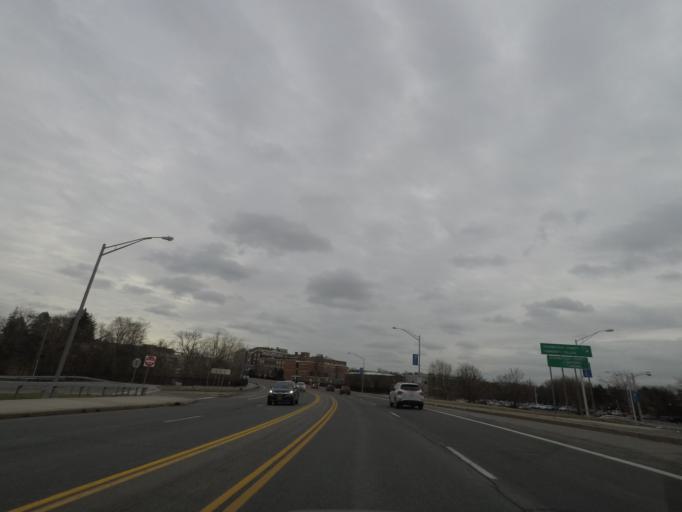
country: US
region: New York
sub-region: Schenectady County
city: Schenectady
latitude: 42.8166
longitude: -73.9528
